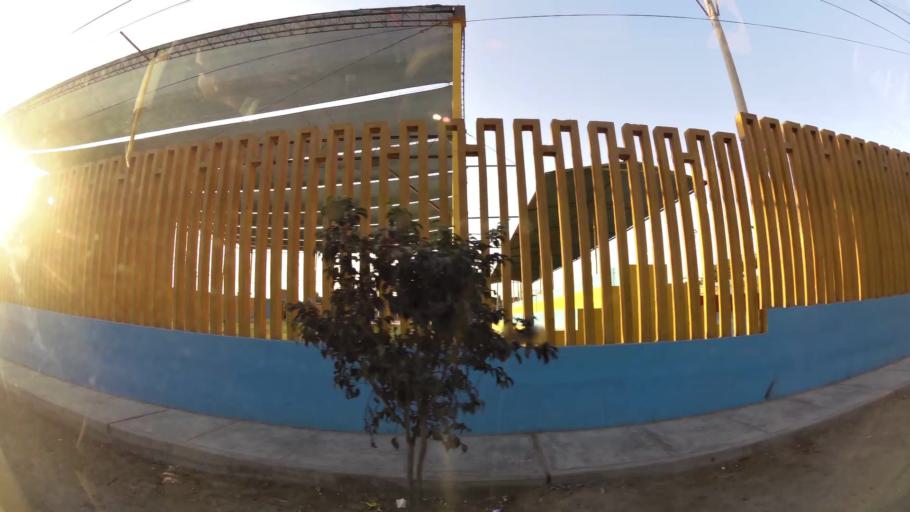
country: PE
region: Ica
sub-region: Provincia de Pisco
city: Villa Tupac Amaru
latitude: -13.7088
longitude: -76.1493
